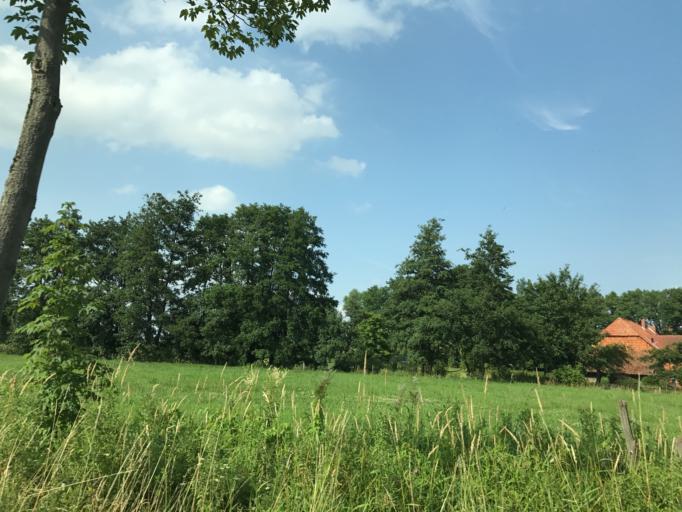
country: DE
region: Lower Saxony
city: Seeburg
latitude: 51.5653
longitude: 10.1406
